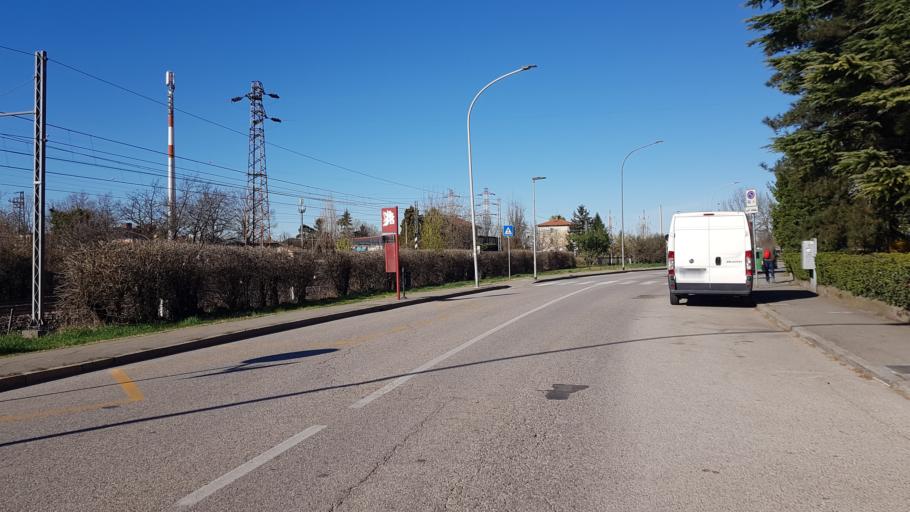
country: IT
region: Emilia-Romagna
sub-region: Provincia di Bologna
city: Bologna
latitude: 44.5207
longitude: 11.3248
